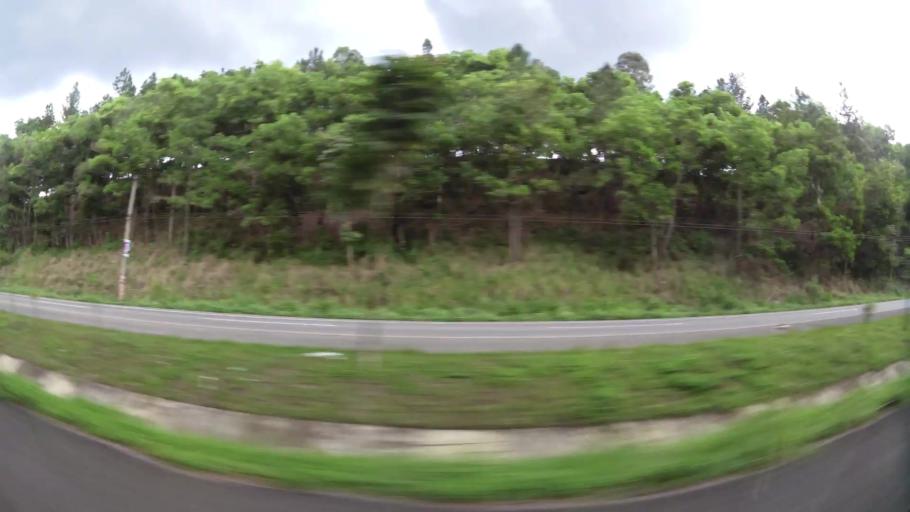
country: DO
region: San Cristobal
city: Villa Altagracia
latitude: 18.7377
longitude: -70.2306
